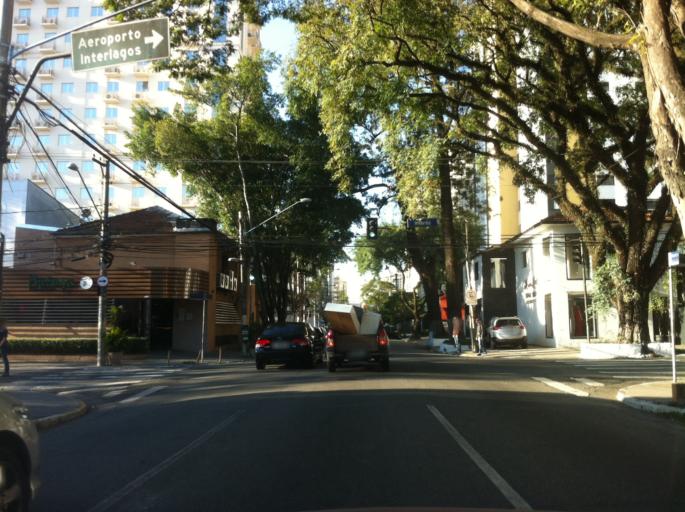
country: BR
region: Sao Paulo
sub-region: Sao Paulo
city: Sao Paulo
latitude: -23.6133
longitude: -46.6653
